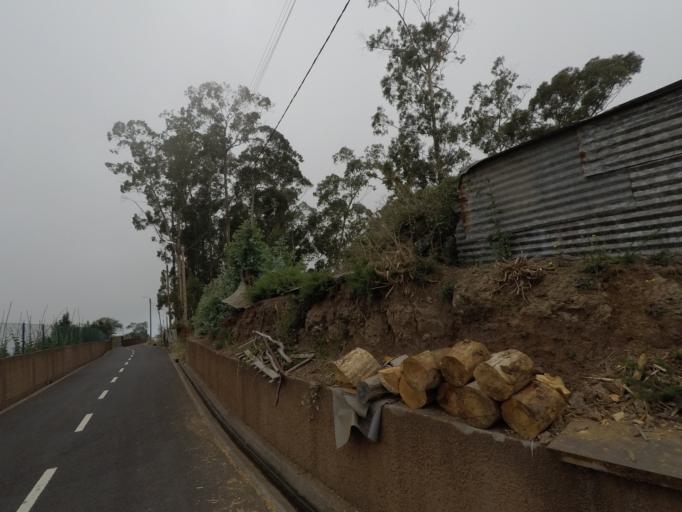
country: PT
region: Madeira
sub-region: Camara de Lobos
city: Curral das Freiras
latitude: 32.6889
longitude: -16.9476
